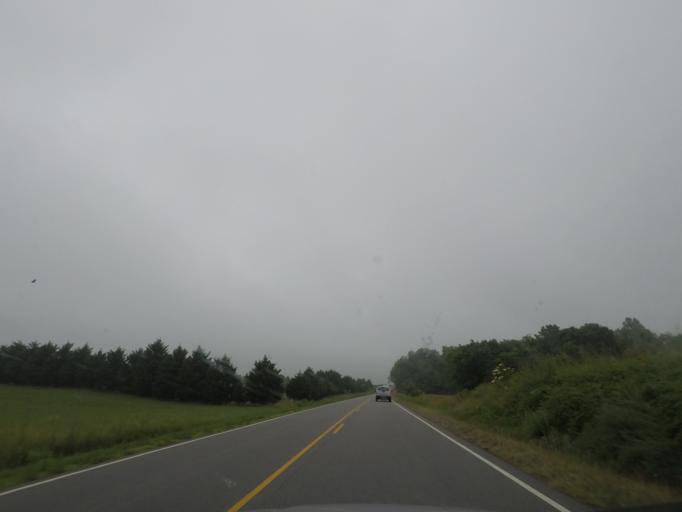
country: US
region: Virginia
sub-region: Prince Edward County
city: Farmville
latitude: 37.3556
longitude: -78.4813
